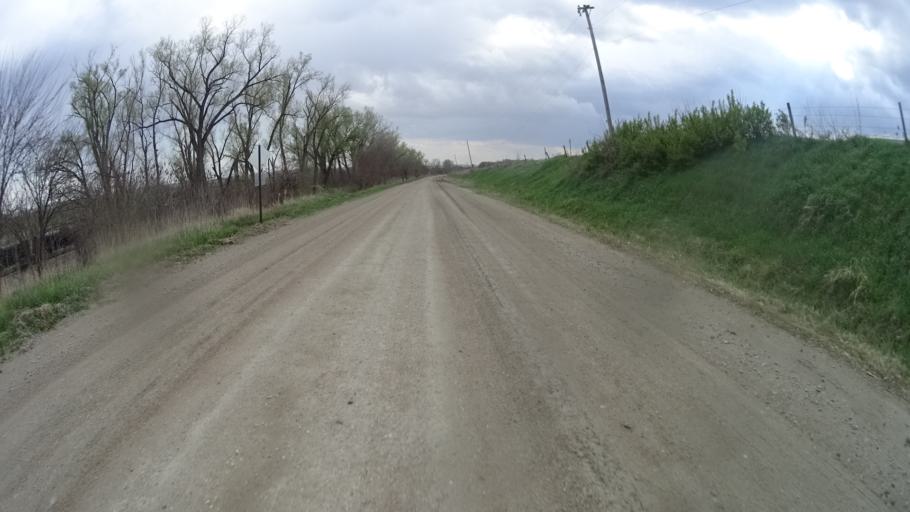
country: US
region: Nebraska
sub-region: Sarpy County
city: Offutt Air Force Base
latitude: 41.0964
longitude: -95.9134
